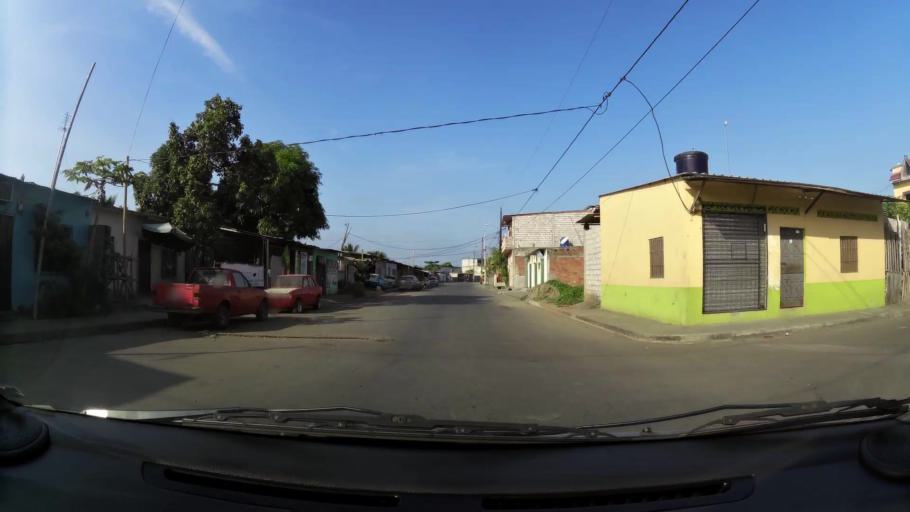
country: EC
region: Guayas
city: Eloy Alfaro
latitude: -2.1843
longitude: -79.8390
